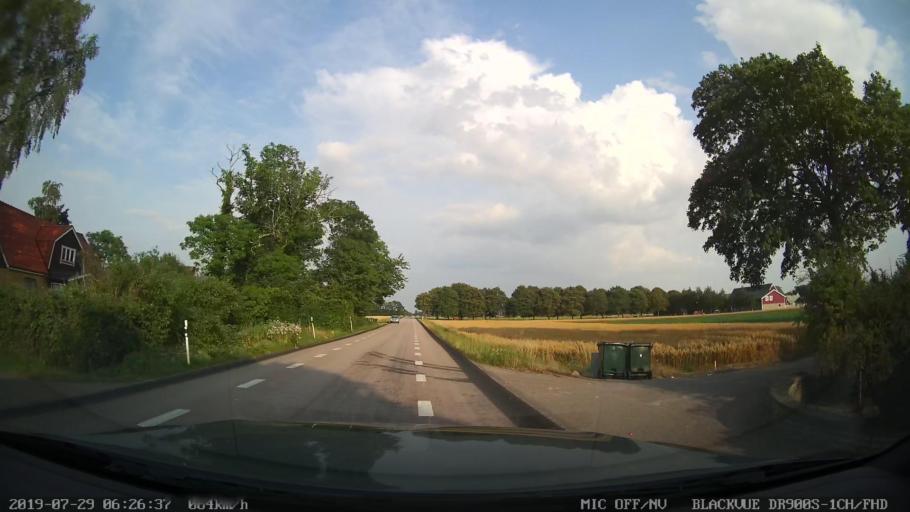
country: SE
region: Skane
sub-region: Helsingborg
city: Odakra
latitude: 56.1105
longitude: 12.7033
